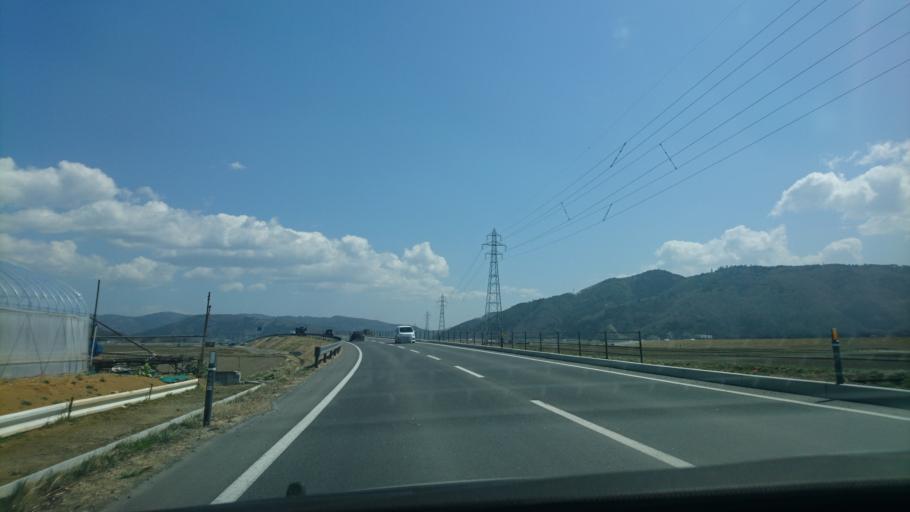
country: JP
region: Miyagi
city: Ishinomaki
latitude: 38.4501
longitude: 141.3197
